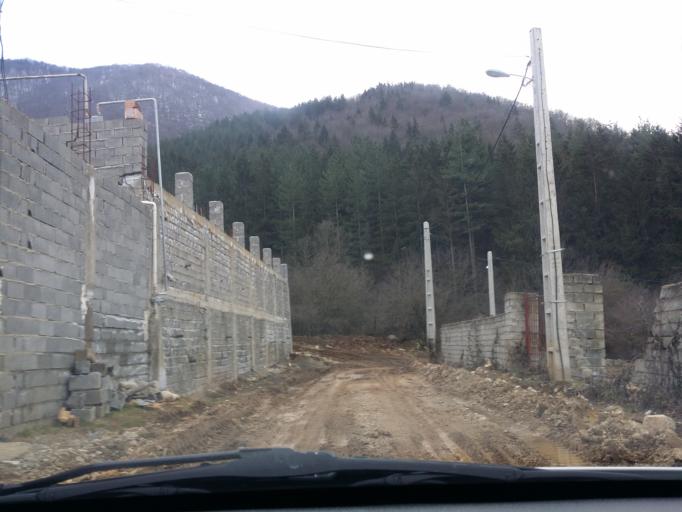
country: IR
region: Mazandaran
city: `Abbasabad
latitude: 36.4969
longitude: 51.1797
